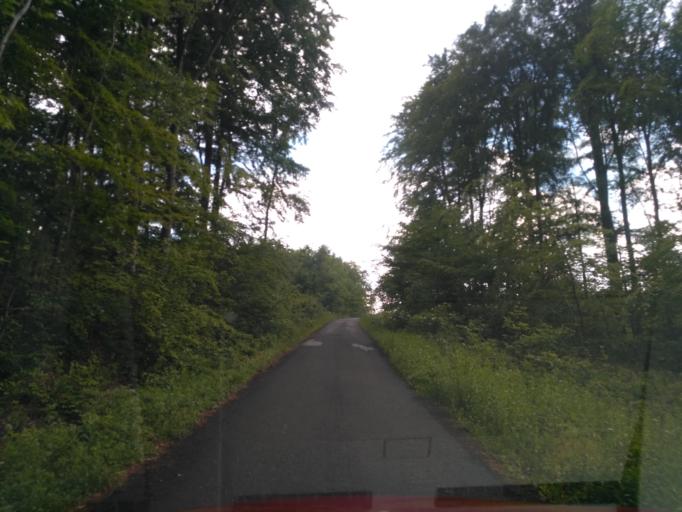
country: SK
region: Presovsky
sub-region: Okres Presov
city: Presov
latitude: 48.9630
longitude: 21.1741
